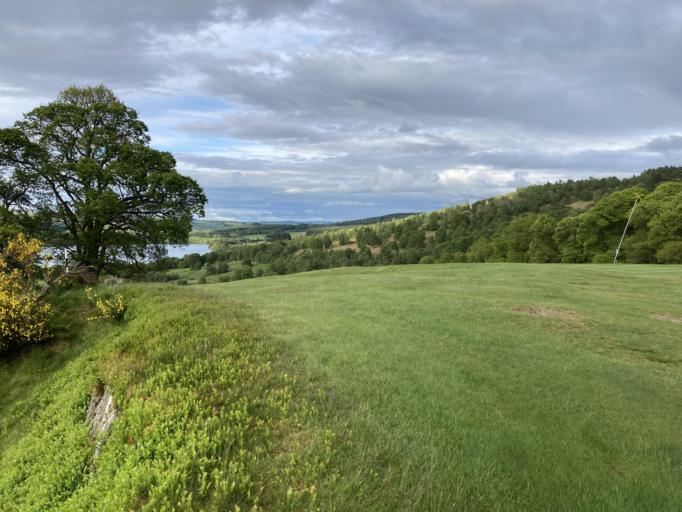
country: GB
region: Scotland
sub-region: Perth and Kinross
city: Bankfoot
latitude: 56.5672
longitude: -3.5712
